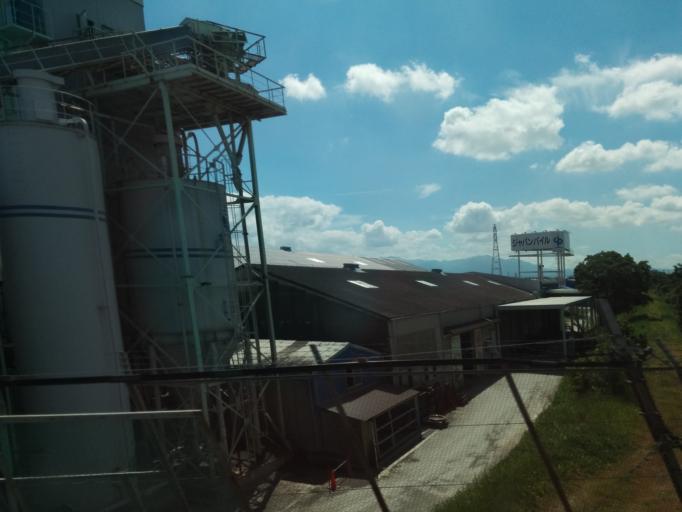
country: JP
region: Shiga Prefecture
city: Youkaichi
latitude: 35.1614
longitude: 136.2028
